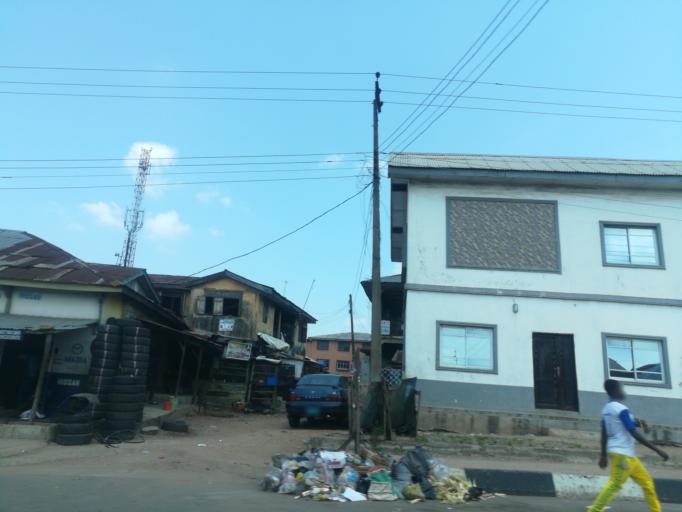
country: NG
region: Ogun
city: Abeokuta
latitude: 7.1521
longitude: 3.3516
